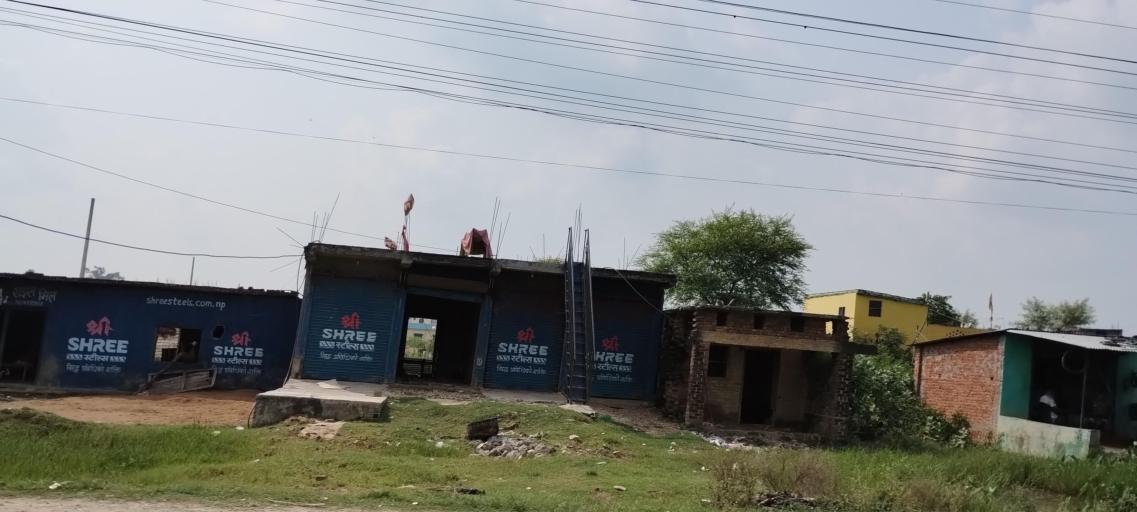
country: NP
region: Mid Western
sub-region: Bheri Zone
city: Nepalgunj
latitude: 28.1555
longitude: 81.6689
